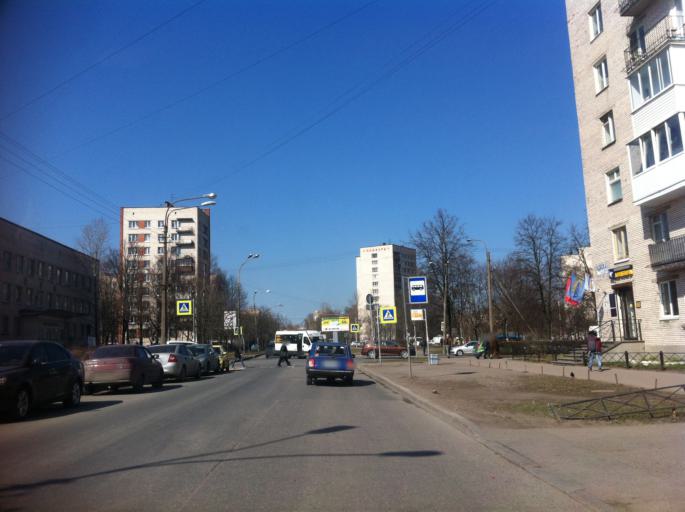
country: RU
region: St.-Petersburg
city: Dachnoye
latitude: 59.8409
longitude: 30.2466
